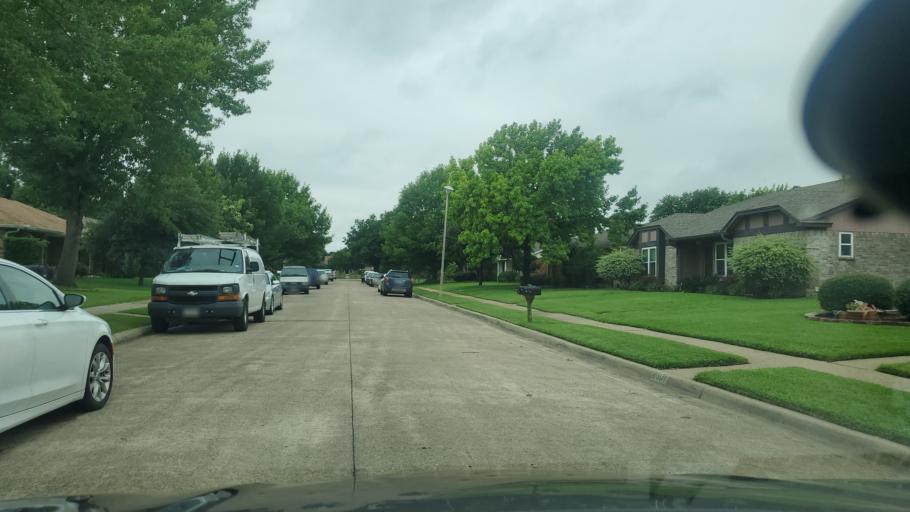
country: US
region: Texas
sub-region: Dallas County
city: Garland
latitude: 32.9401
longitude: -96.6330
